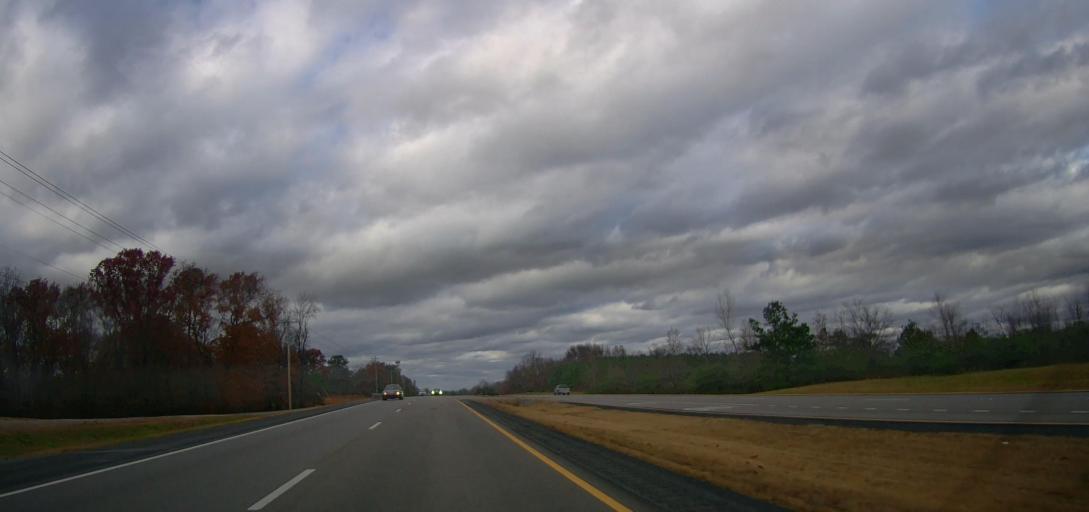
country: US
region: Alabama
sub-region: Morgan County
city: Falkville
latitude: 34.2759
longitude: -86.9943
